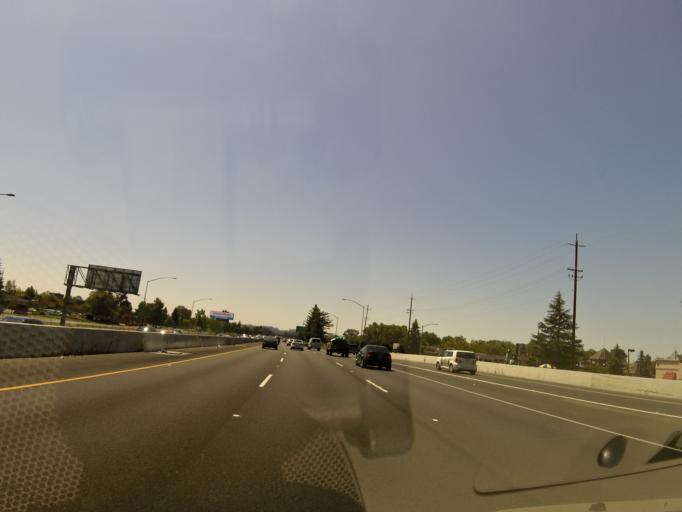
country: US
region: California
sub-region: Sonoma County
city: Rohnert Park
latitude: 38.3605
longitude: -122.7132
